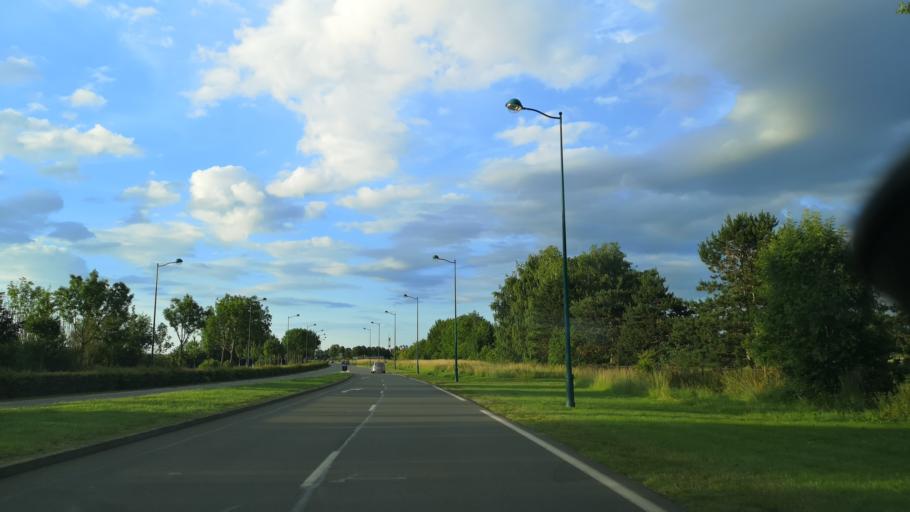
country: FR
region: Ile-de-France
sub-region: Departement de Seine-et-Marne
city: Magny-le-Hongre
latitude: 48.8576
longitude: 2.8045
